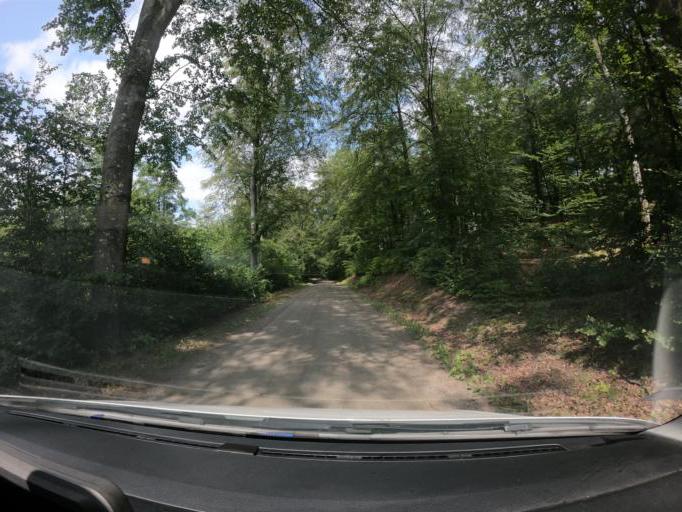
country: SE
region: Skane
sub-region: Hassleholms Kommun
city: Sosdala
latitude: 55.9797
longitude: 13.6484
